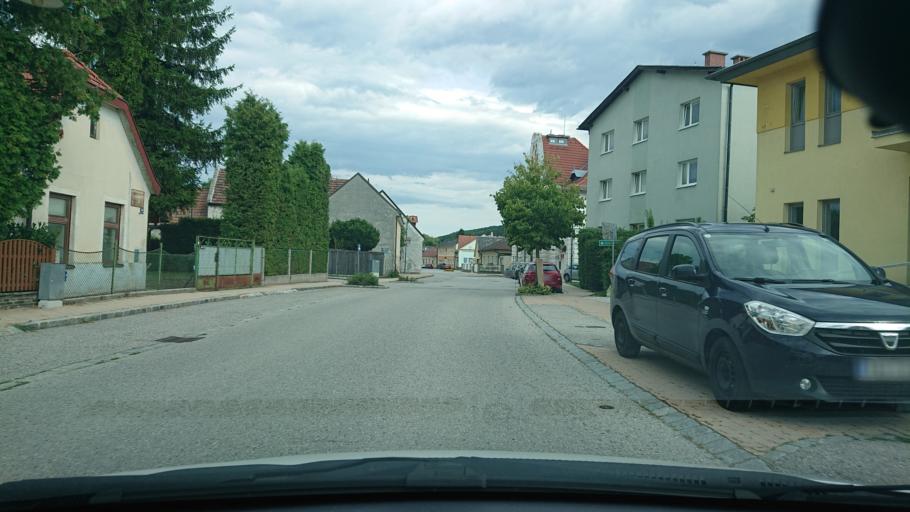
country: AT
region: Lower Austria
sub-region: Politischer Bezirk Baden
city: Hirtenberg
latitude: 47.9384
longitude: 16.1497
